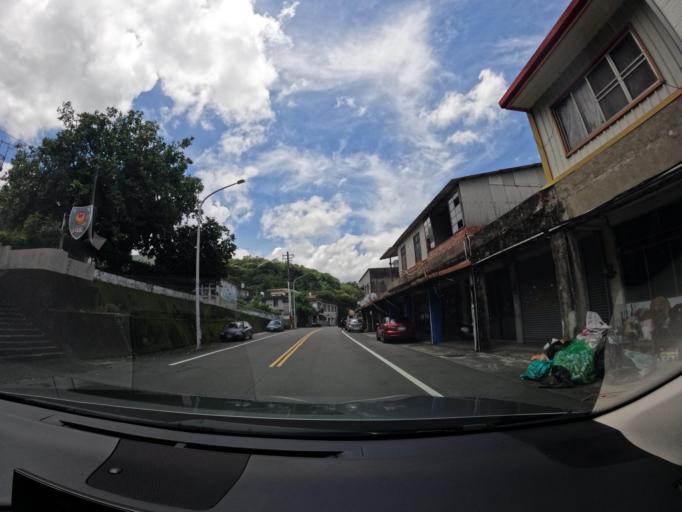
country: TW
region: Taiwan
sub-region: Hsinchu
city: Hsinchu
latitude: 24.6292
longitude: 121.0114
